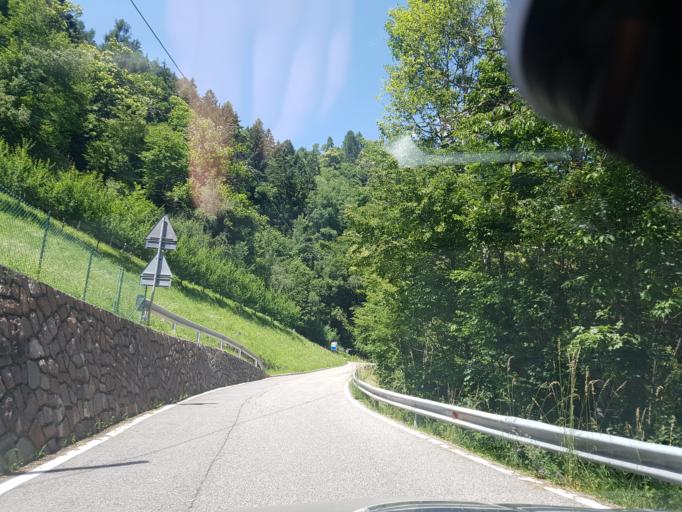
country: IT
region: Trentino-Alto Adige
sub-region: Bolzano
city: Villandro
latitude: 46.6247
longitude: 11.5380
